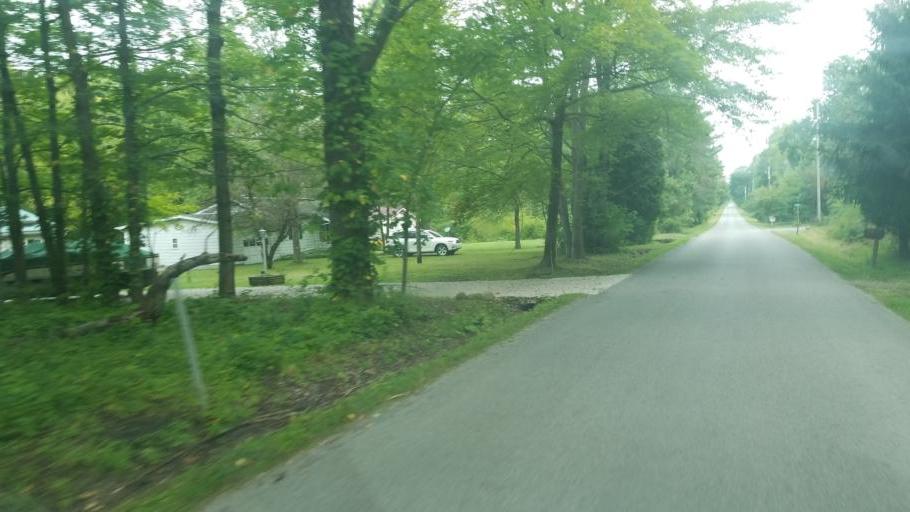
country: US
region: Pennsylvania
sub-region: Crawford County
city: Pymatuning Central
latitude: 41.6190
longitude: -80.5000
